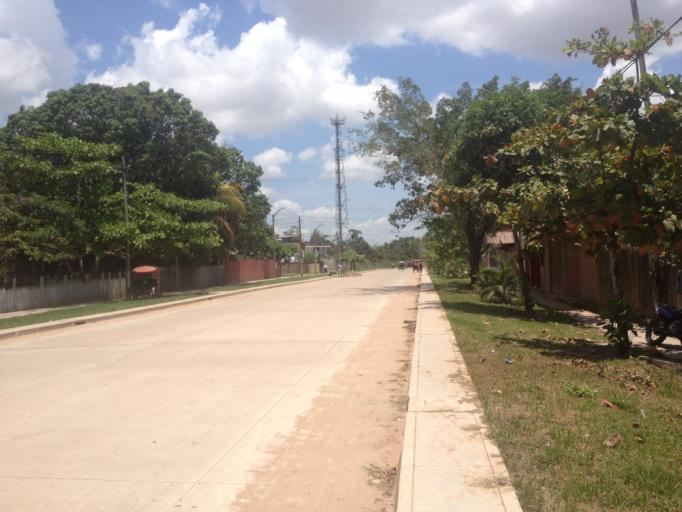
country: PE
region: Ucayali
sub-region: Provincia de Coronel Portillo
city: Pucallpa
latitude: -8.3728
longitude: -74.5674
